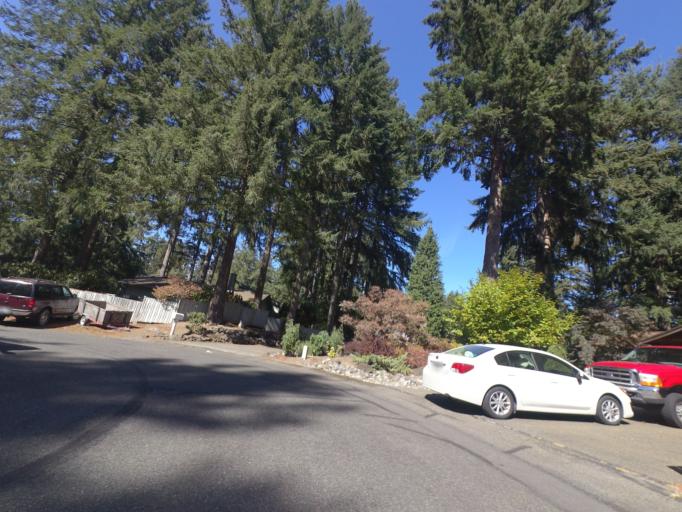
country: US
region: Washington
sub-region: Pierce County
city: Fircrest
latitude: 47.2150
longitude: -122.5202
